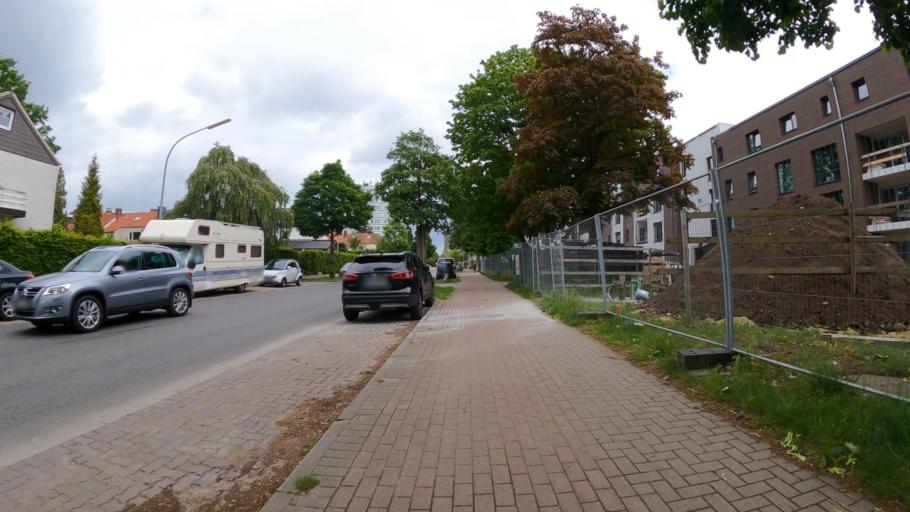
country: DE
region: Schleswig-Holstein
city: Norderstedt
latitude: 53.7047
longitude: 10.0042
